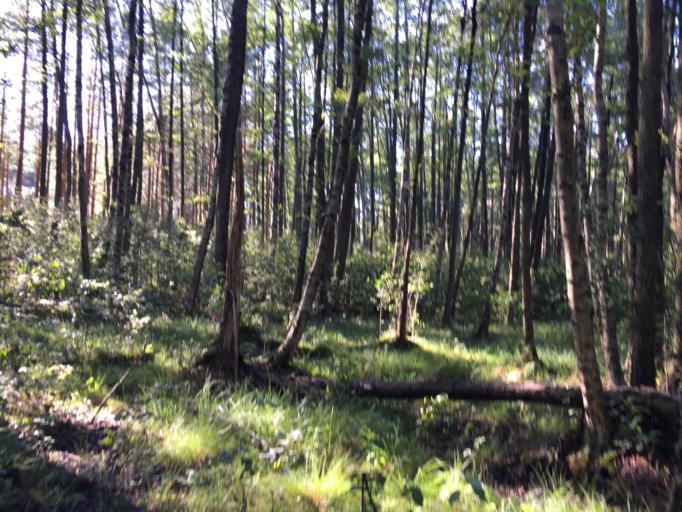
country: LV
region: Riga
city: Jaunciems
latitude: 57.0672
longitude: 24.1347
